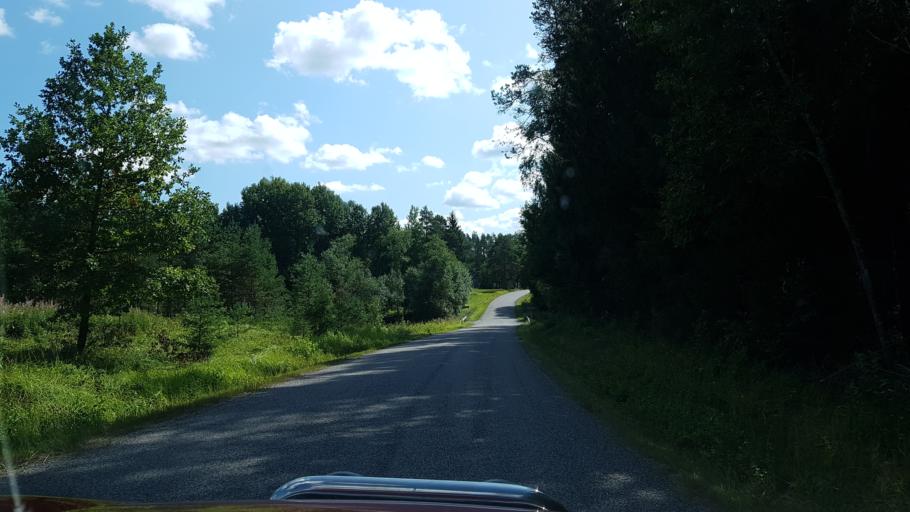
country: EE
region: Vorumaa
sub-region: Voru linn
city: Voru
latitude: 57.7328
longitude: 27.2076
